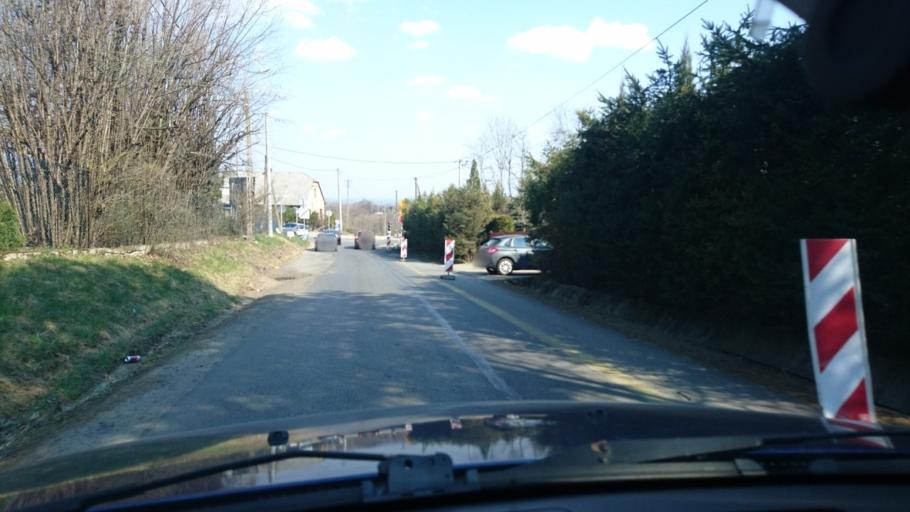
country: PL
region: Silesian Voivodeship
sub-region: Powiat bielski
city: Kozy
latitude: 49.8226
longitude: 19.1153
